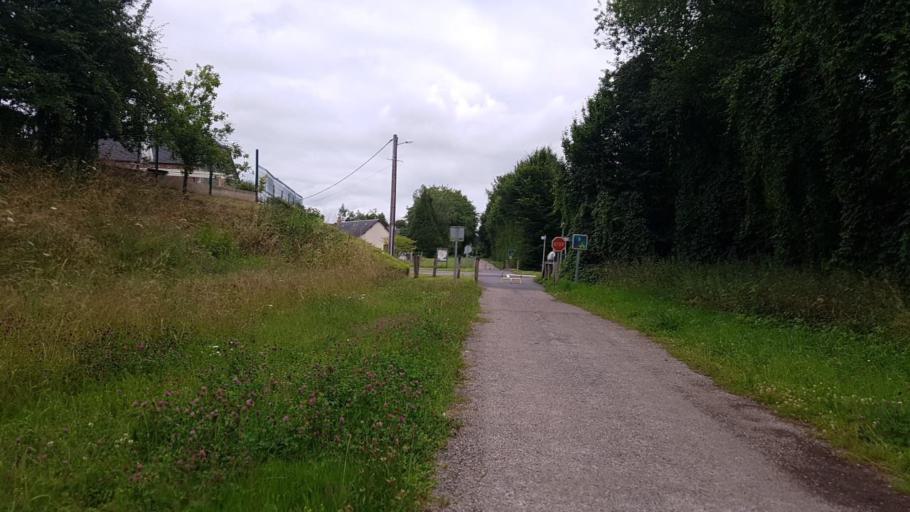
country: FR
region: Picardie
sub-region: Departement de l'Aisne
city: Origny-en-Thierache
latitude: 49.9285
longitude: 4.0303
